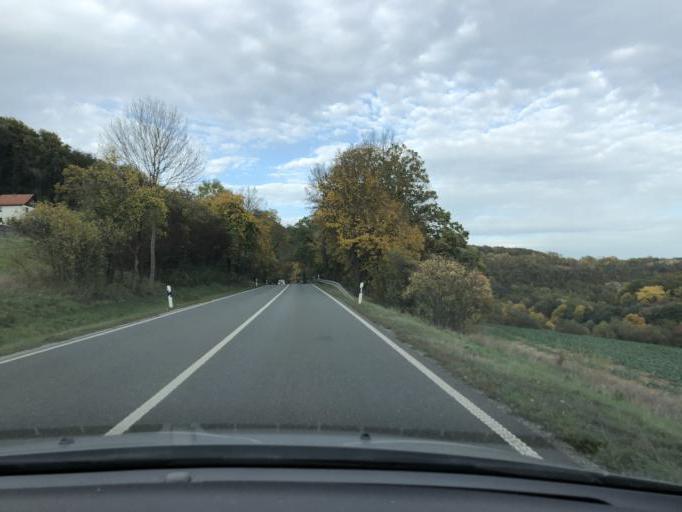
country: DE
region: Thuringia
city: Bad Berka
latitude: 50.9095
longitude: 11.2782
